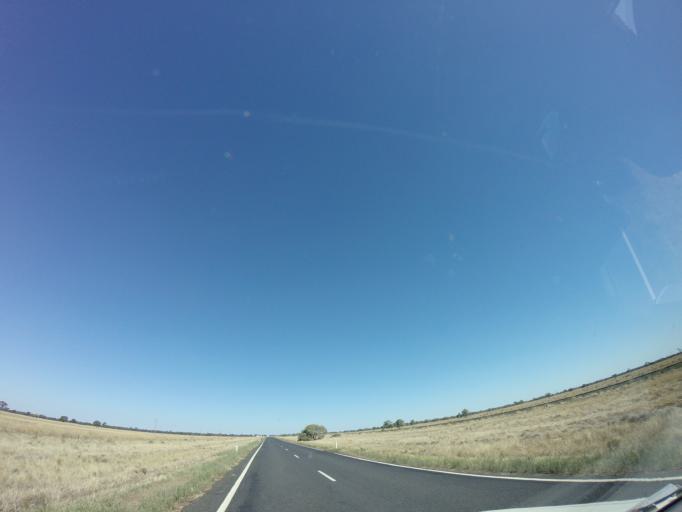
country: AU
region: New South Wales
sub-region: Bogan
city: Nyngan
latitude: -31.6737
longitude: 147.4073
